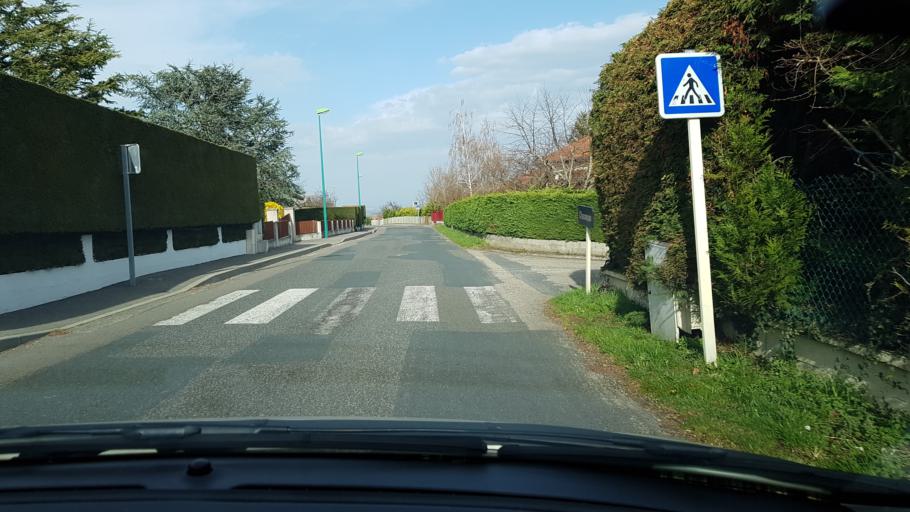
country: FR
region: Rhone-Alpes
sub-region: Departement du Rhone
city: Saint-Maurice-sur-Dargoire
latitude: 45.5814
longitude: 4.6339
